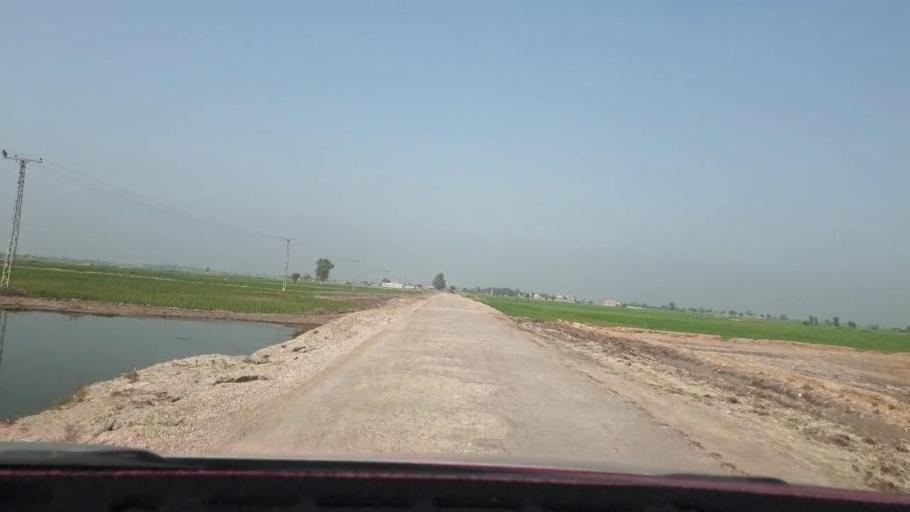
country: PK
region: Sindh
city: Nasirabad
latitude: 27.4243
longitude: 67.9209
